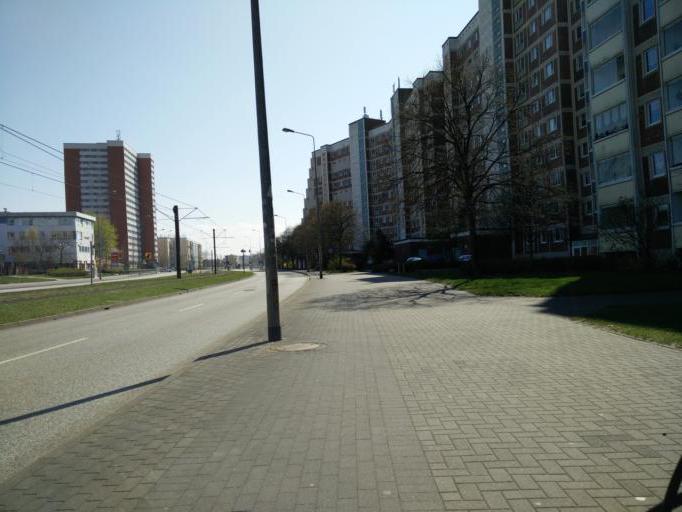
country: DE
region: Mecklenburg-Vorpommern
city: Lambrechtshagen
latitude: 54.1207
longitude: 12.0582
